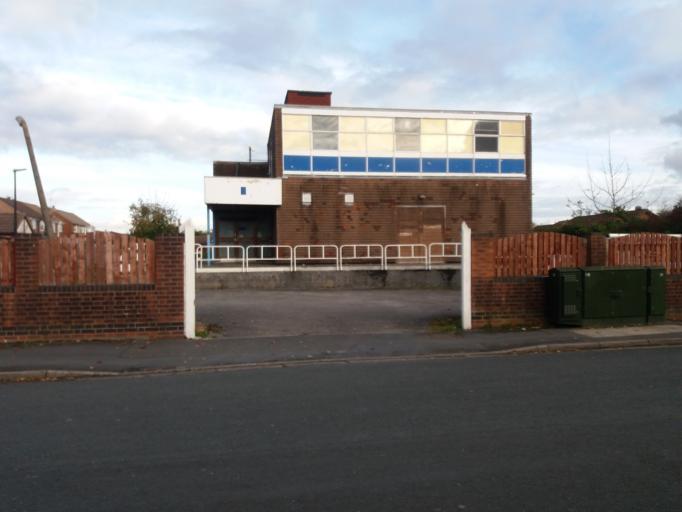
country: GB
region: England
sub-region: Lancashire
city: Coppull
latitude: 53.6199
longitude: -2.6636
